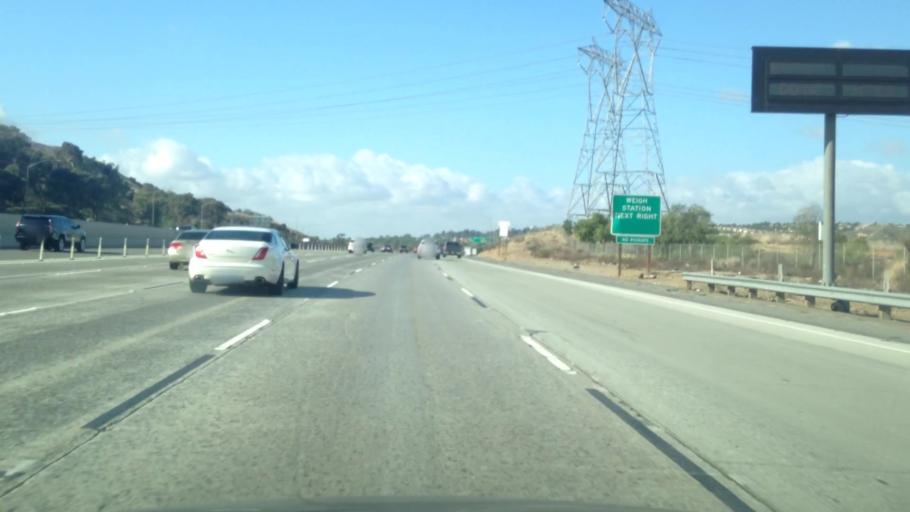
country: US
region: California
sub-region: Orange County
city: Yorba Linda
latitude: 33.8698
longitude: -117.7502
